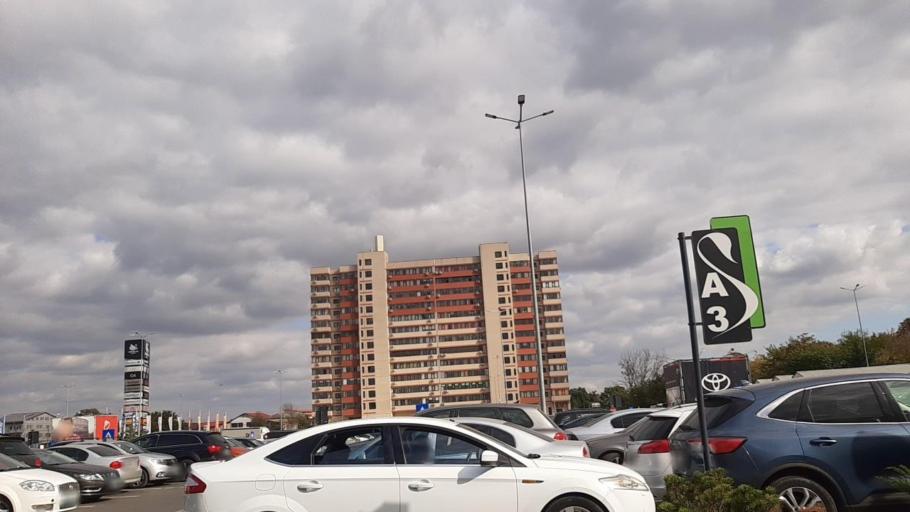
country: RO
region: Galati
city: Galati
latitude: 45.4520
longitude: 28.0321
